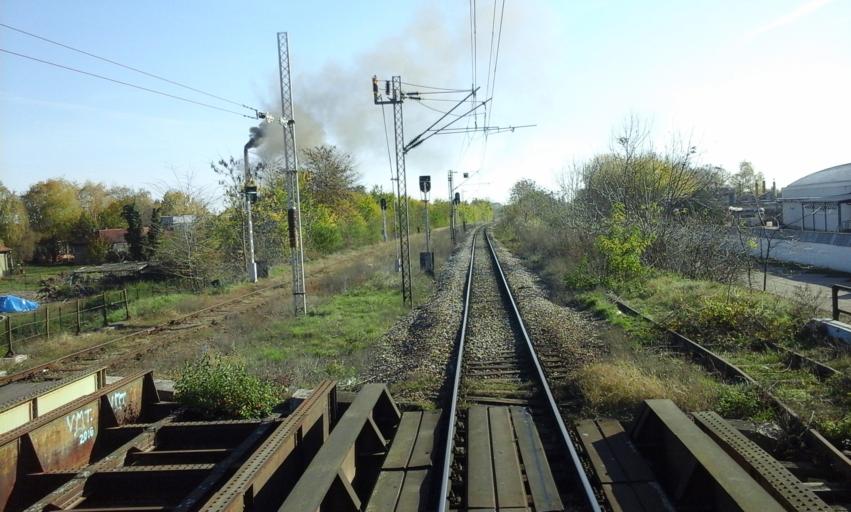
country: RS
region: Autonomna Pokrajina Vojvodina
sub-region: Severnobacki Okrug
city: Subotica
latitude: 46.0914
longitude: 19.6833
